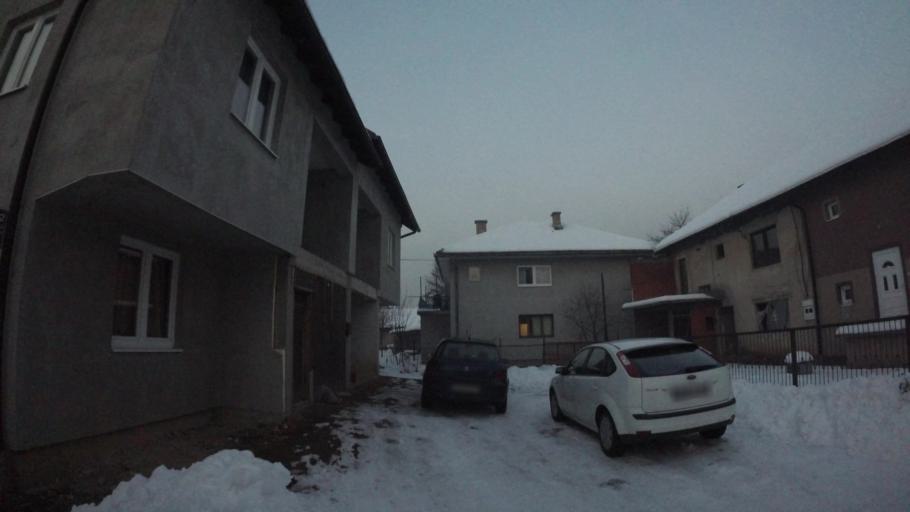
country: BA
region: Federation of Bosnia and Herzegovina
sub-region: Kanton Sarajevo
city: Sarajevo
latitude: 43.8333
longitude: 18.3195
